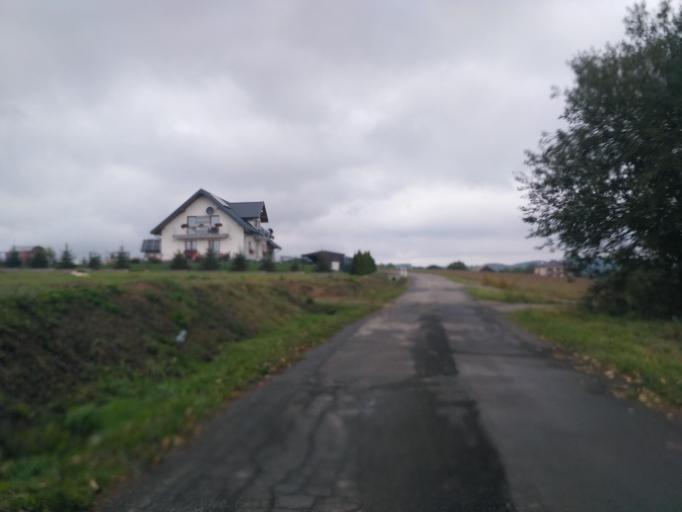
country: PL
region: Subcarpathian Voivodeship
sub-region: Powiat debicki
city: Brzostek
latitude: 49.9250
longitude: 21.4470
